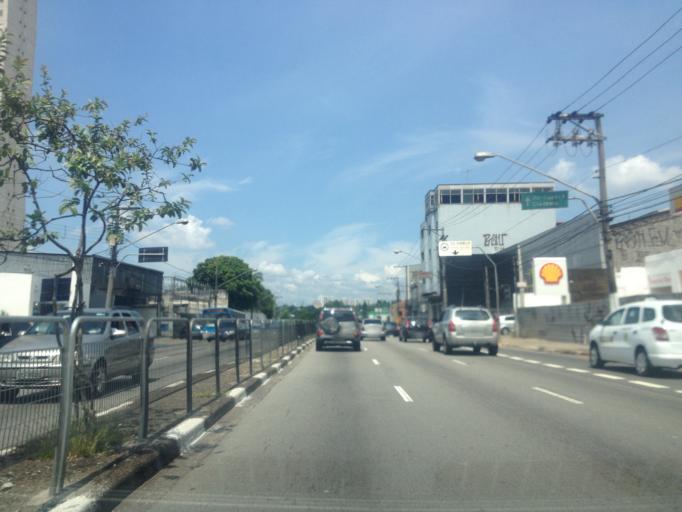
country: BR
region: Sao Paulo
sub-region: Diadema
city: Diadema
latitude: -23.6386
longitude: -46.6725
